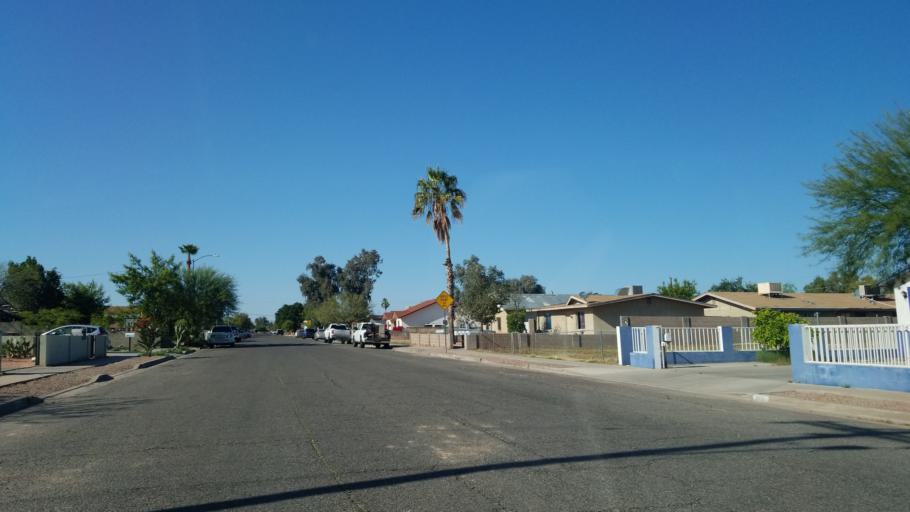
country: US
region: Arizona
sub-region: Maricopa County
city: Glendale
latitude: 33.5332
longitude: -112.1750
